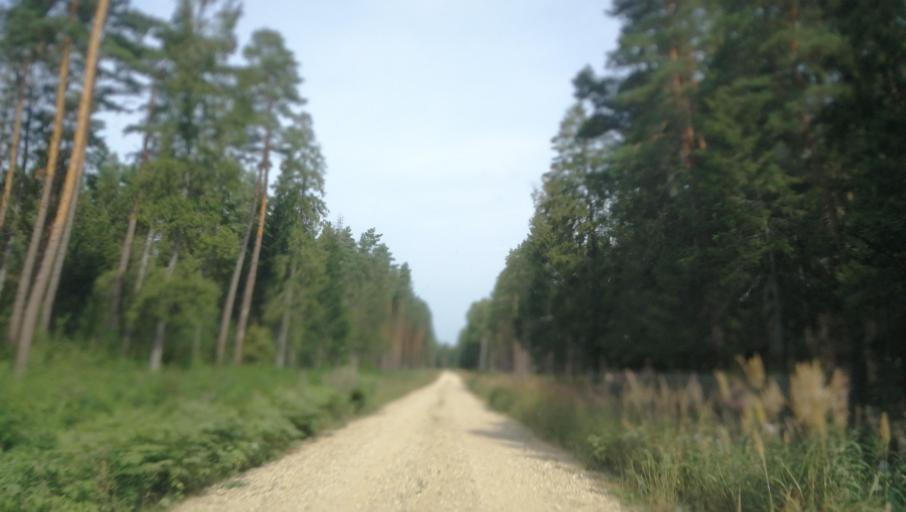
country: LV
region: Pavilostas
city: Pavilosta
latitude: 56.8085
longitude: 21.3371
